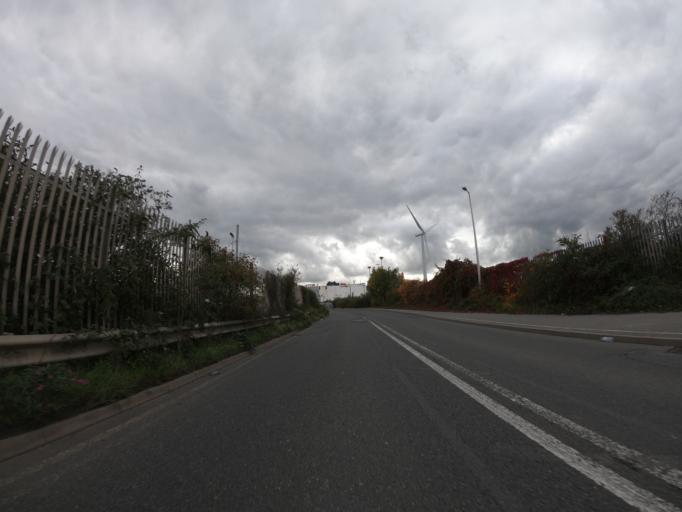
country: GB
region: England
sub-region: Borough of Thurrock
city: Tilbury
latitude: 51.4541
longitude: 0.3636
